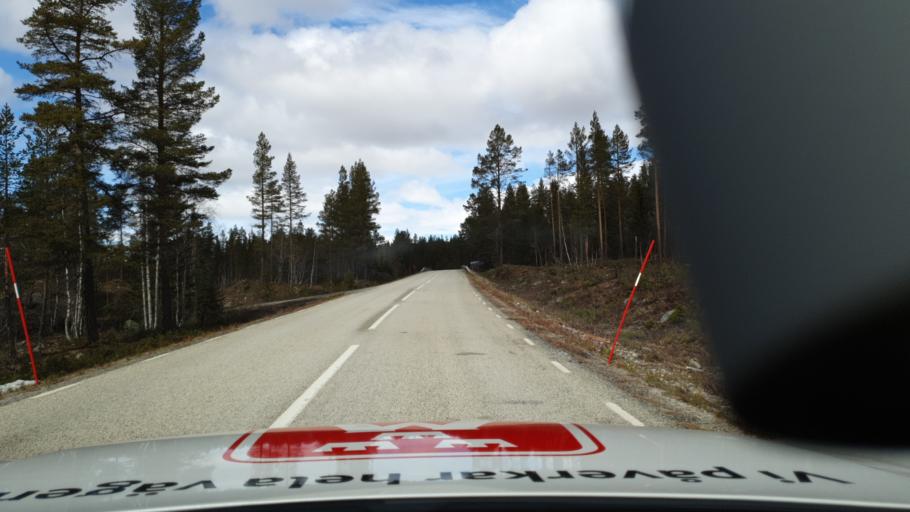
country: SE
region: Jaemtland
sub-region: Are Kommun
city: Jarpen
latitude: 62.8347
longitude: 13.4236
